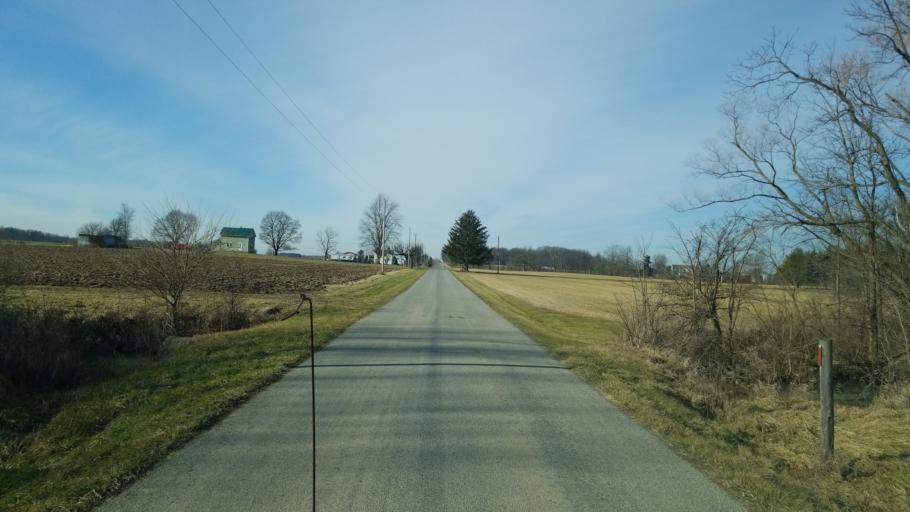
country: US
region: Ohio
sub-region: Hardin County
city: Ada
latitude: 40.8125
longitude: -83.8884
